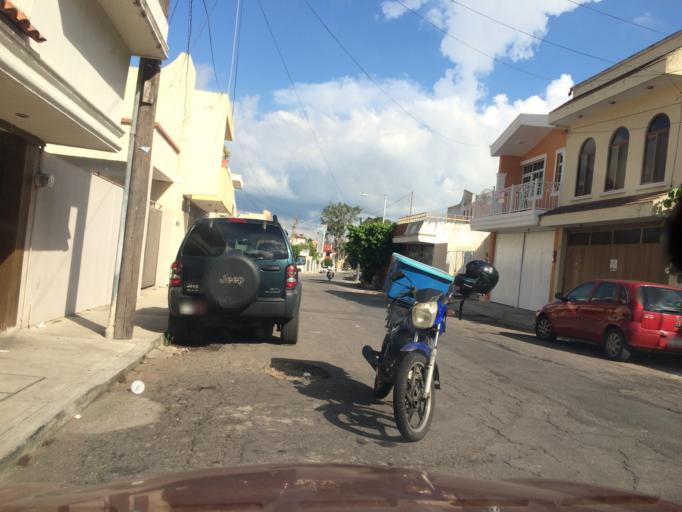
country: MX
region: Nayarit
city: Tepic
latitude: 21.5094
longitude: -104.9049
